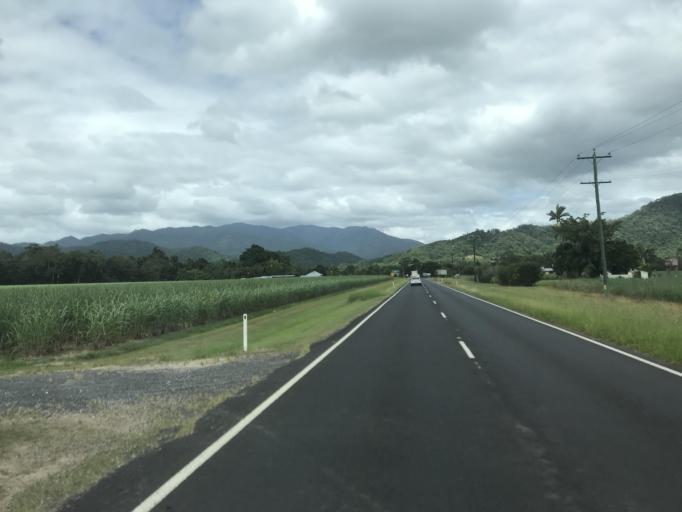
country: AU
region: Queensland
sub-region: Cassowary Coast
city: Innisfail
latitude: -17.8095
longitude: 146.0106
